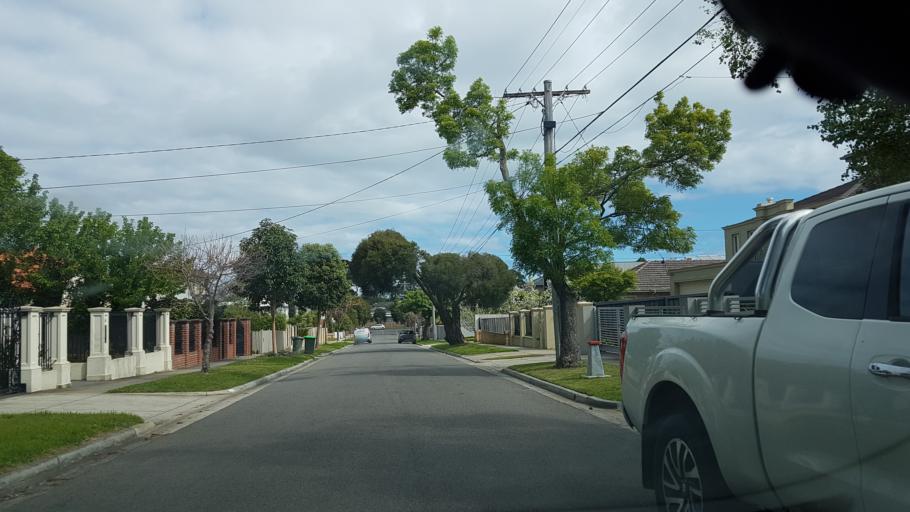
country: AU
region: Victoria
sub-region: Bayside
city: Hampton East
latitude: -37.9294
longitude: 145.0201
